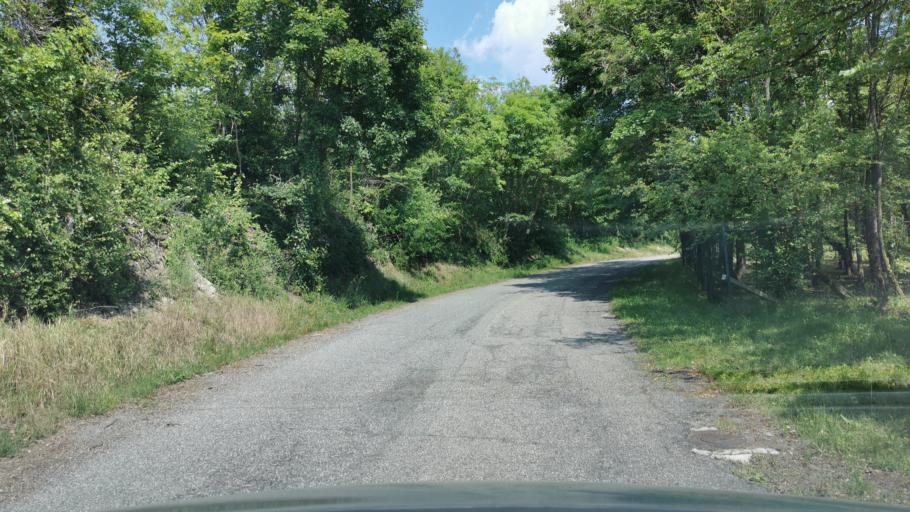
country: IT
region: Piedmont
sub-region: Provincia di Asti
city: Grazzano Badoglio
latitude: 45.0533
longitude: 8.3188
